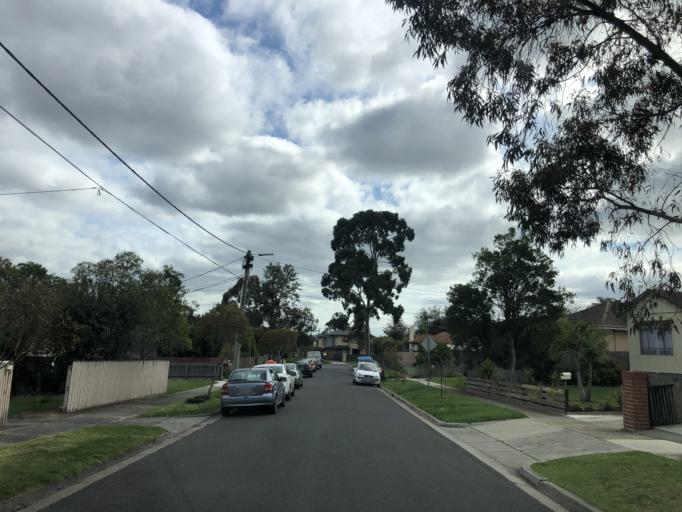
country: AU
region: Victoria
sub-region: Monash
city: Ashwood
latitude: -37.8754
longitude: 145.0974
